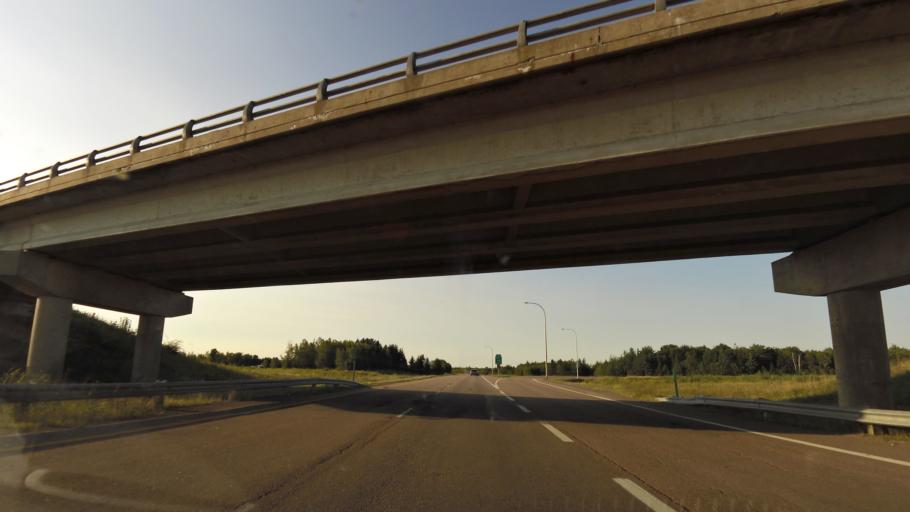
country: CA
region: New Brunswick
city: Dieppe
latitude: 46.1007
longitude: -64.6063
